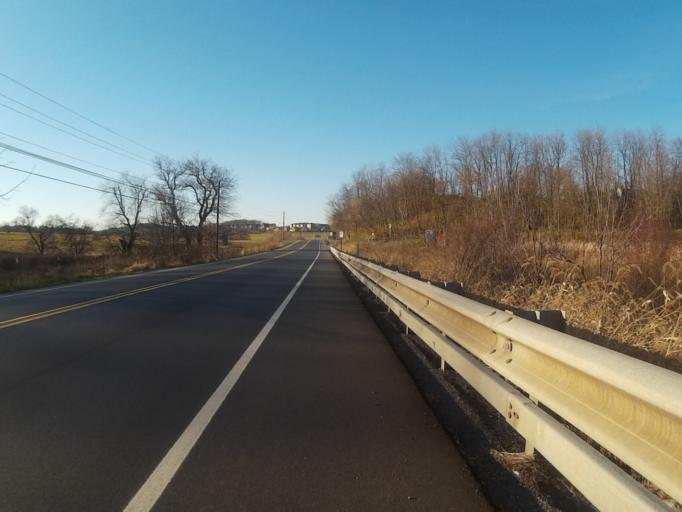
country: US
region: Pennsylvania
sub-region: Centre County
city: State College
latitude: 40.8192
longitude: -77.8616
